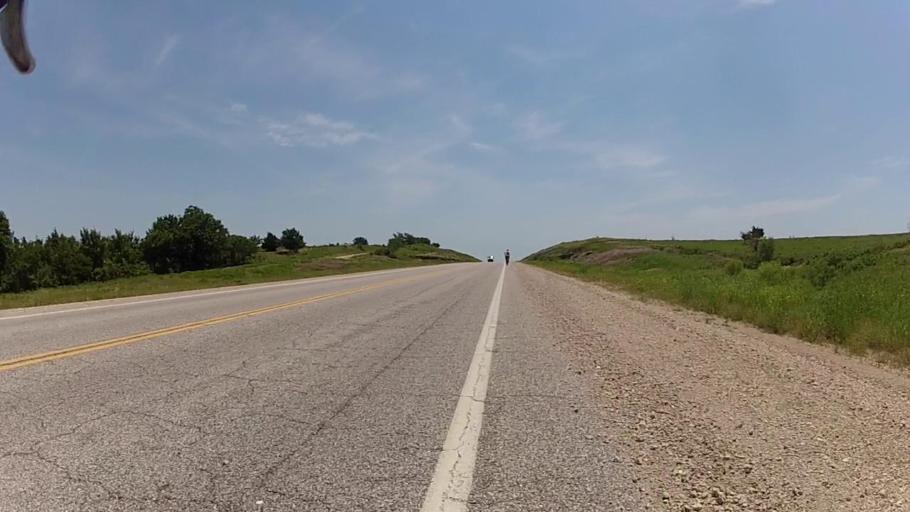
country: US
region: Kansas
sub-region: Chautauqua County
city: Sedan
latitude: 37.1131
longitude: -96.4412
